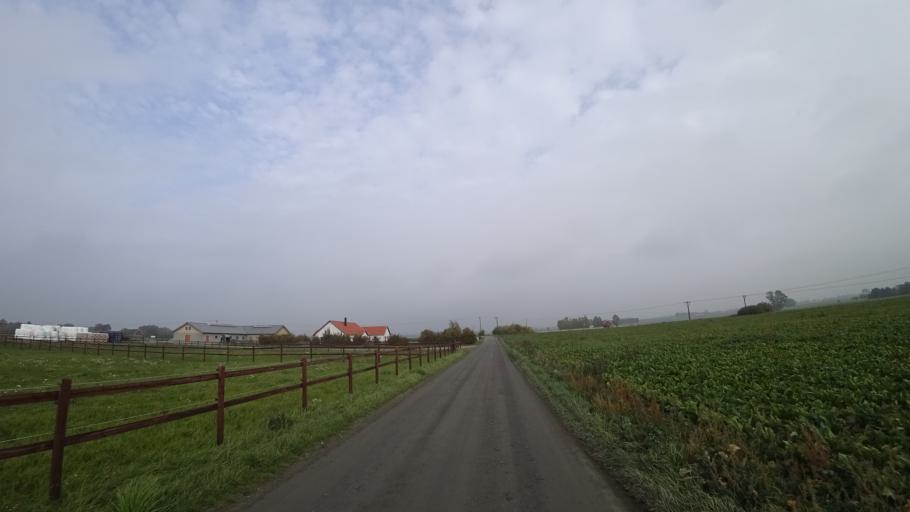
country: SE
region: Skane
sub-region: Kavlinge Kommun
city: Loddekopinge
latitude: 55.8085
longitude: 13.0053
